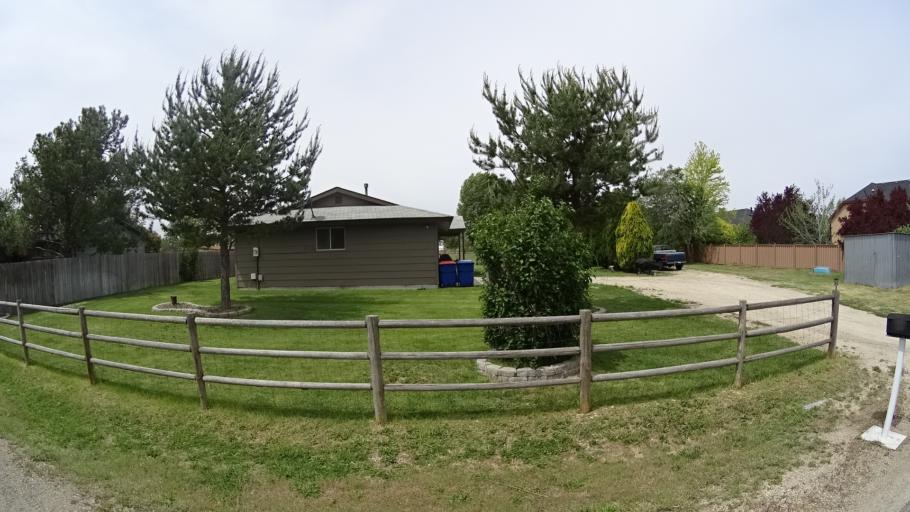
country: US
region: Idaho
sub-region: Ada County
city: Meridian
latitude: 43.5573
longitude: -116.3244
